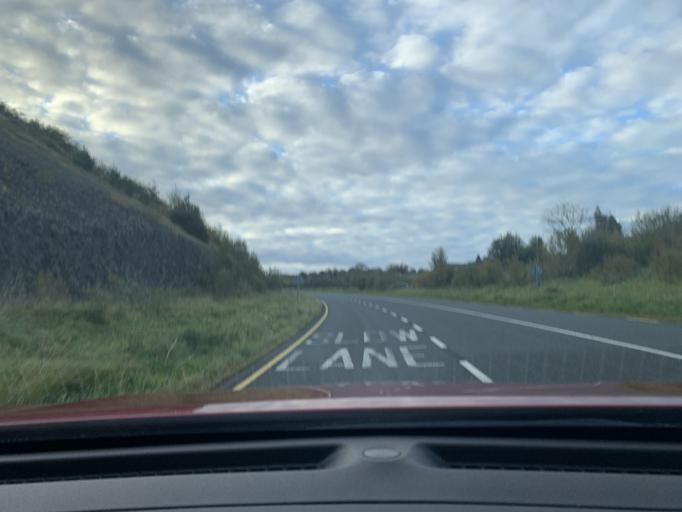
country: IE
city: Ballisodare
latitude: 54.2258
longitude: -8.4704
